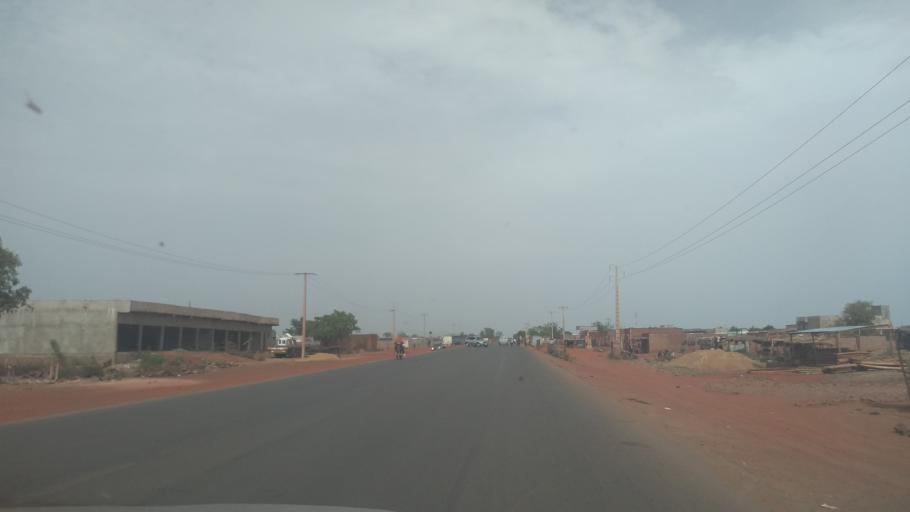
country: ML
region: Bamako
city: Bamako
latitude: 12.5848
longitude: -7.8252
